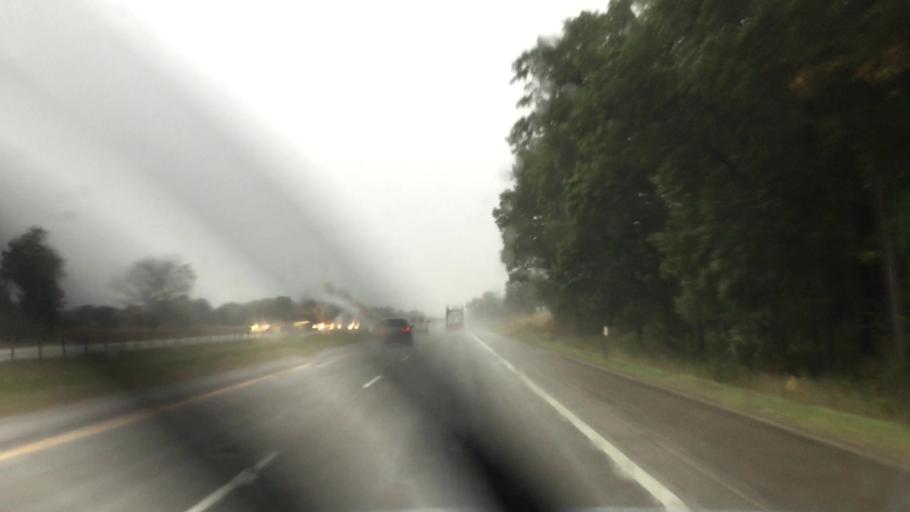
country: US
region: Michigan
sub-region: Van Buren County
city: Mattawan
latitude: 42.2208
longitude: -85.8151
